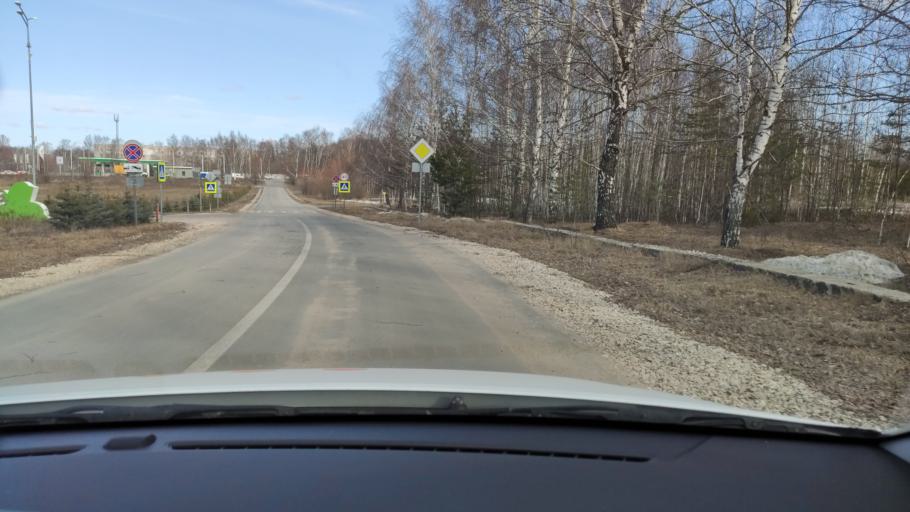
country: RU
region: Tatarstan
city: Osinovo
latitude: 55.8438
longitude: 48.9163
